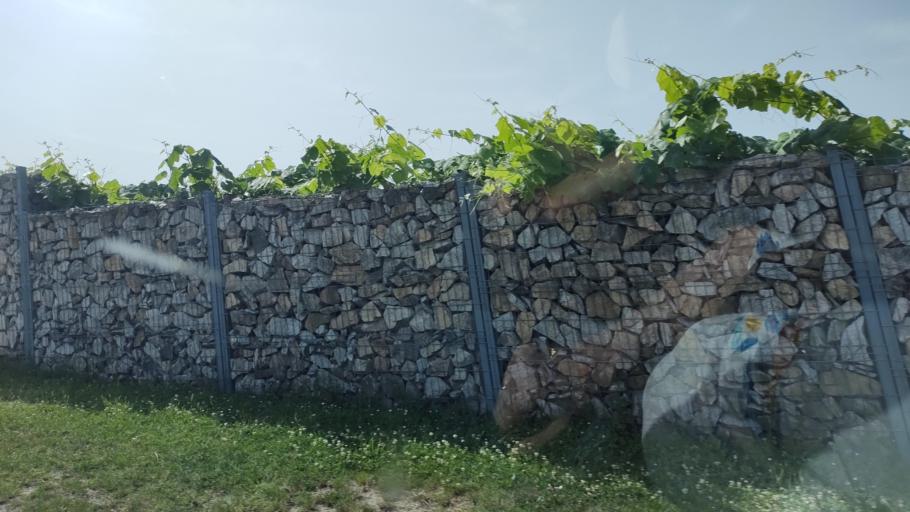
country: RO
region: Mehedinti
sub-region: Comuna Eselnita
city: Eselnita
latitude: 44.6827
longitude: 22.3427
